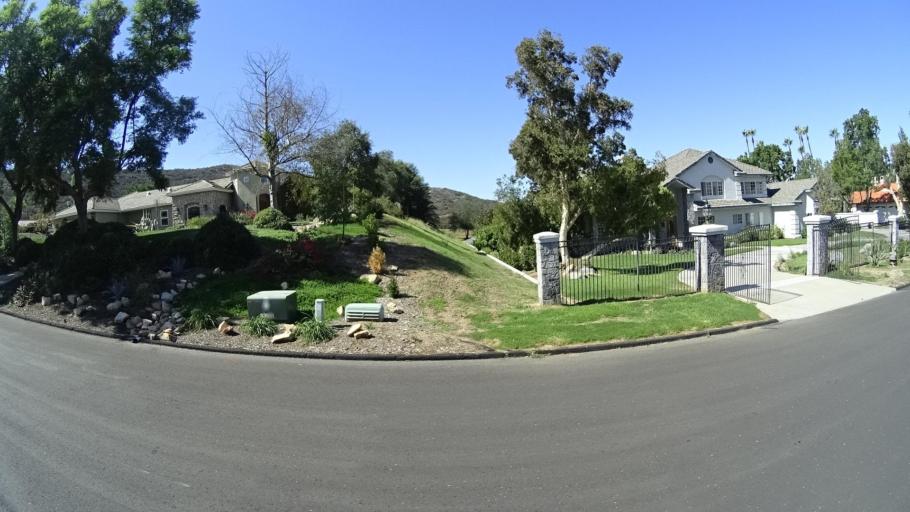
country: US
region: California
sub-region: San Diego County
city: Rancho San Diego
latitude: 32.7374
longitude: -116.9181
